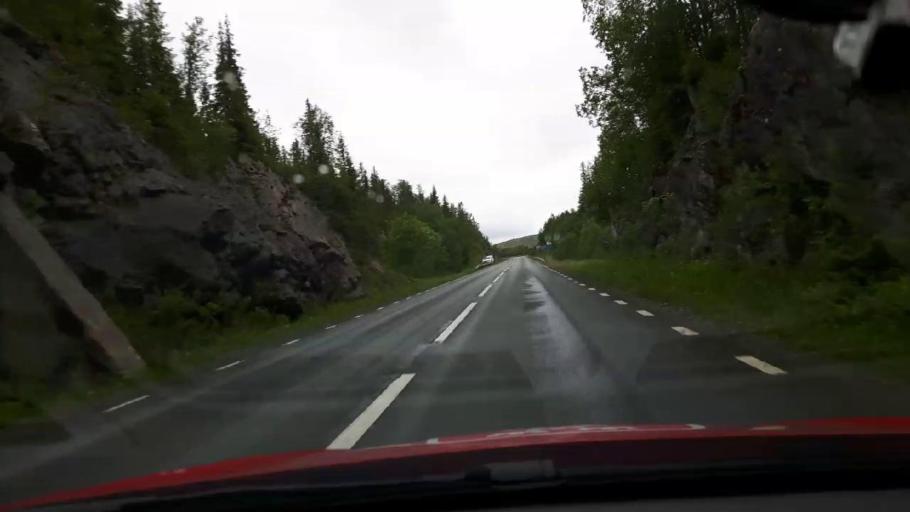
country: NO
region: Nord-Trondelag
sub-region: Meraker
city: Meraker
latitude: 63.3328
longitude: 12.0611
